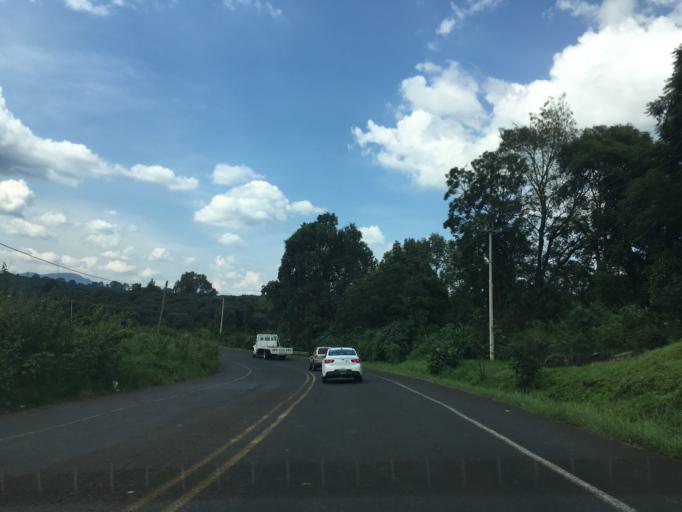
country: MX
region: Michoacan
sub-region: Tingueindin
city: Tingueindin
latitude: 19.7480
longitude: -102.4858
